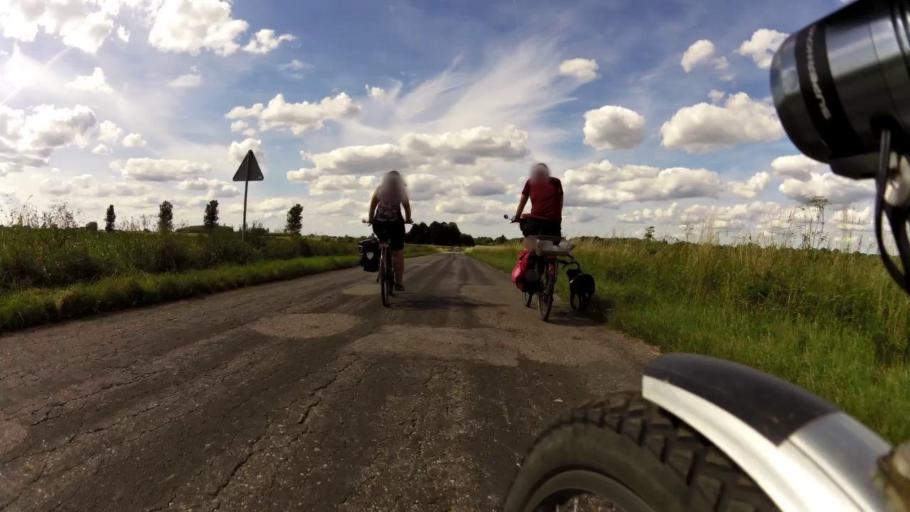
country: PL
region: West Pomeranian Voivodeship
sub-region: Powiat lobeski
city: Dobra
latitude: 53.5773
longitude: 15.3999
